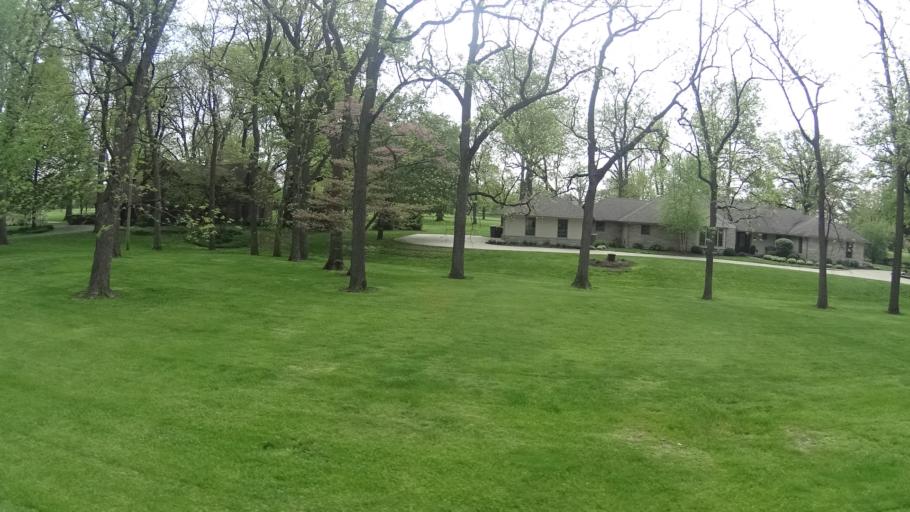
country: US
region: Indiana
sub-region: Madison County
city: Anderson
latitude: 40.1263
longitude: -85.6916
